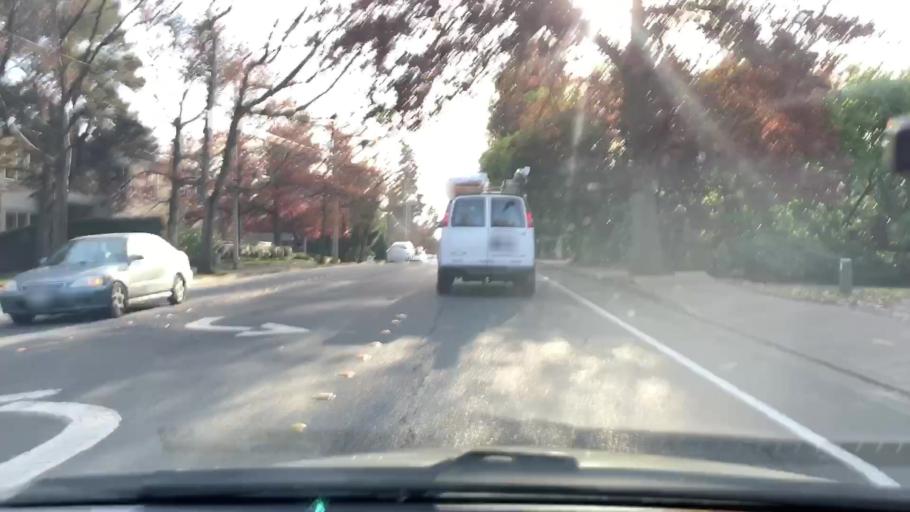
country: US
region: Washington
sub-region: King County
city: Bellevue
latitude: 47.6249
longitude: -122.1910
